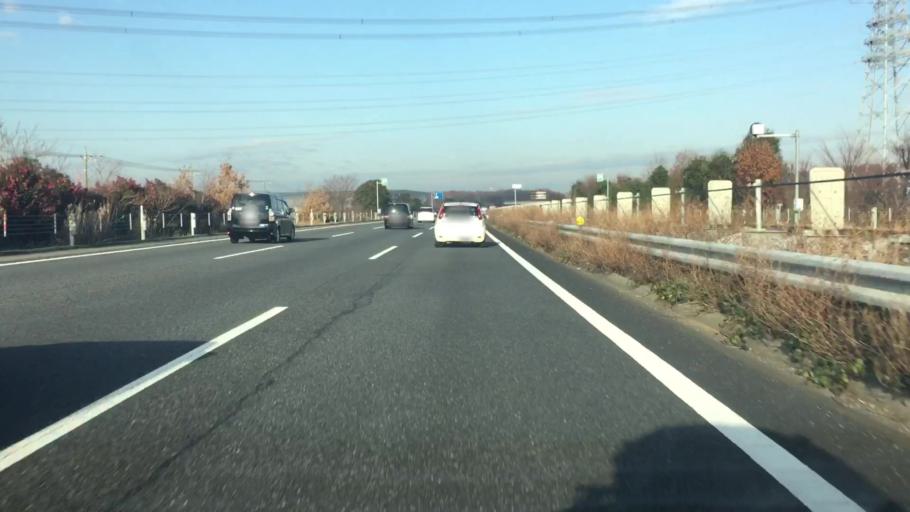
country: JP
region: Saitama
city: Honjo
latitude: 36.2029
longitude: 139.1782
